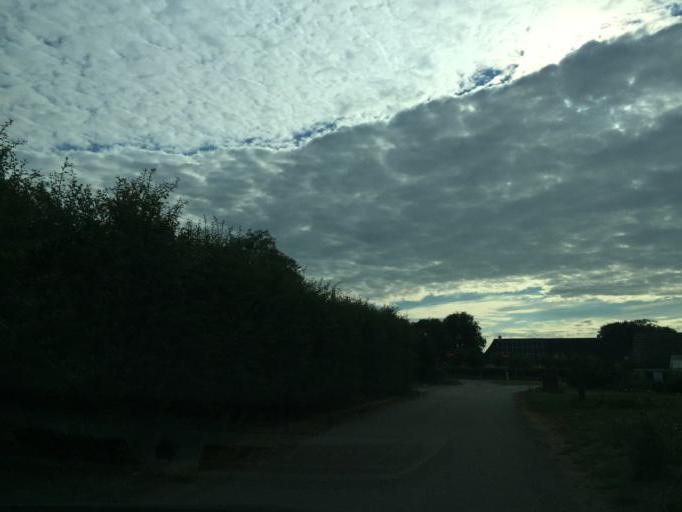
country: DK
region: South Denmark
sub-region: Assens Kommune
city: Assens
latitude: 55.2733
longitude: 9.9754
